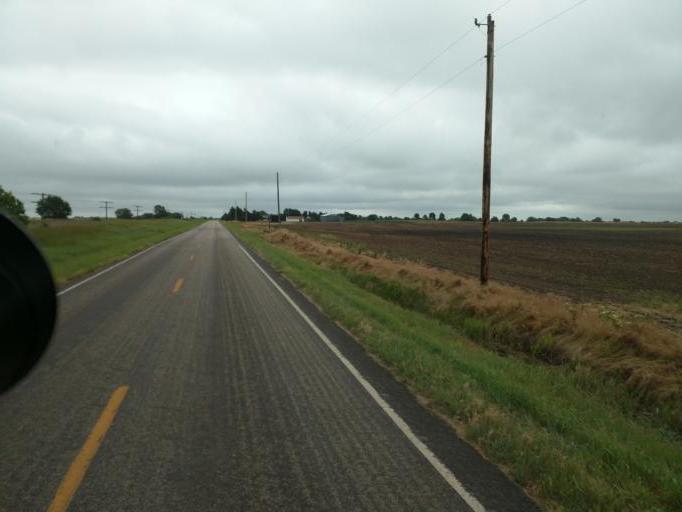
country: US
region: Kansas
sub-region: Reno County
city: Nickerson
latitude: 37.9703
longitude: -98.1231
